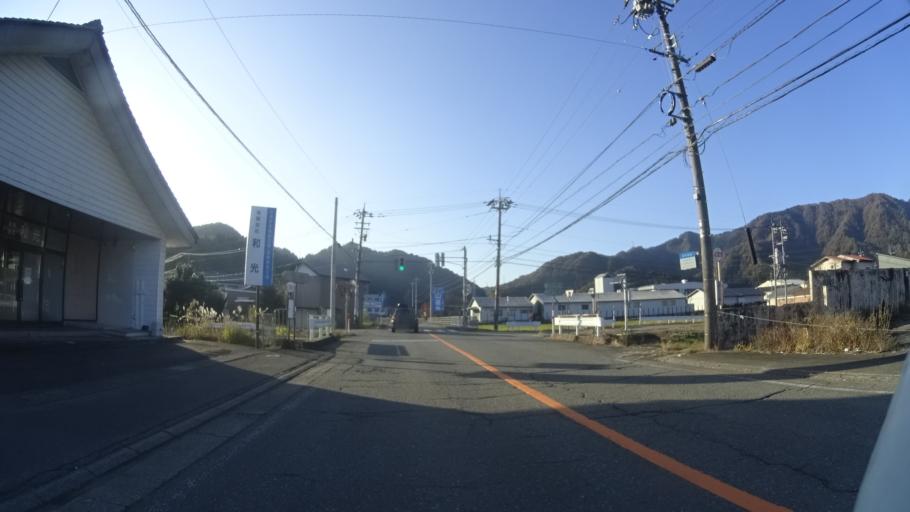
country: JP
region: Fukui
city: Ono
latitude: 35.9937
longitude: 136.4685
